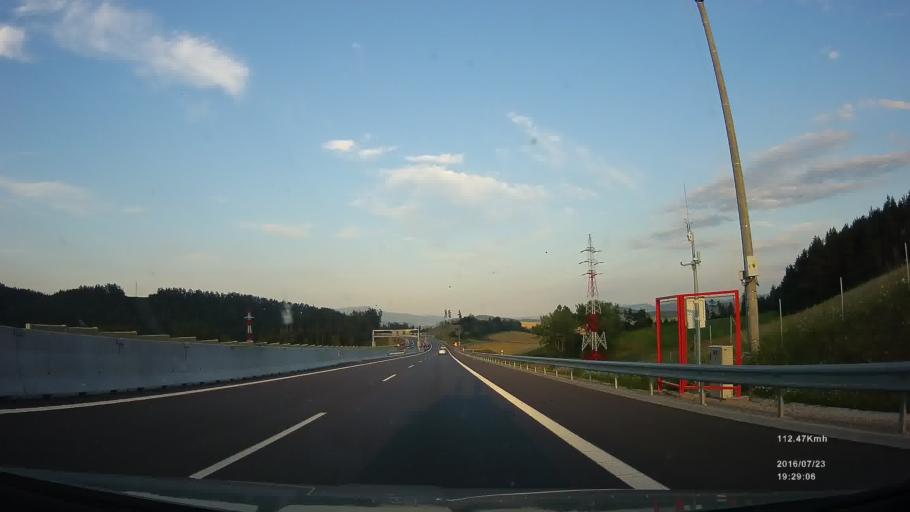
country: SK
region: Presovsky
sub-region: Okres Presov
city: Levoca
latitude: 49.0087
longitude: 20.6224
